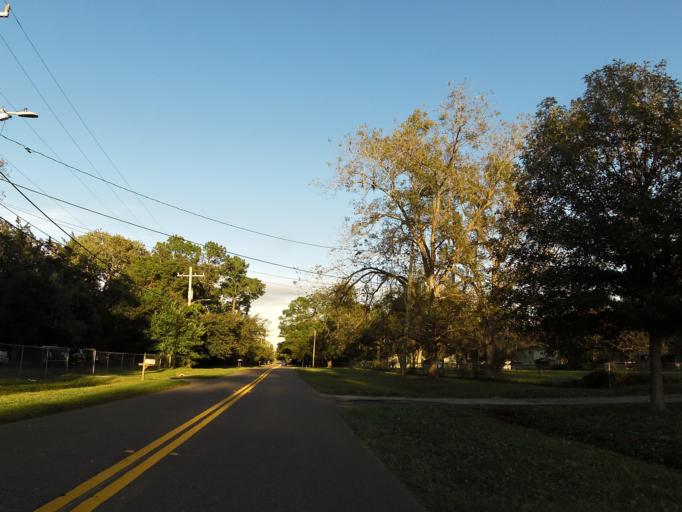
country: US
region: Florida
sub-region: Duval County
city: Jacksonville
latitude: 30.3658
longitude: -81.7482
